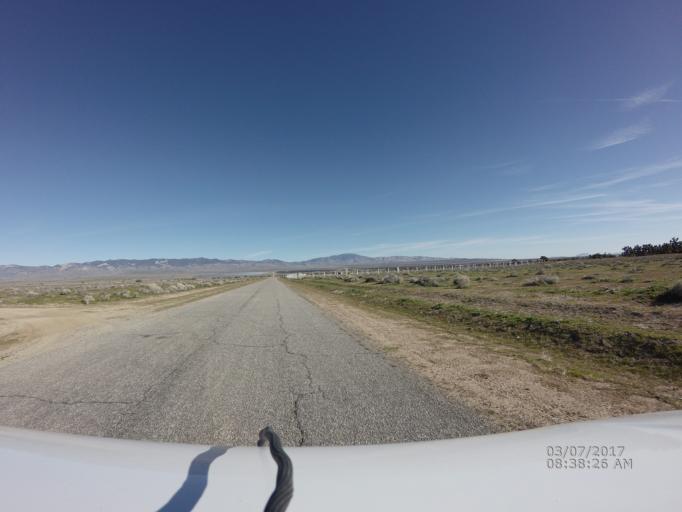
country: US
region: California
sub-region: Los Angeles County
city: Green Valley
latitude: 34.7986
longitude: -118.5457
